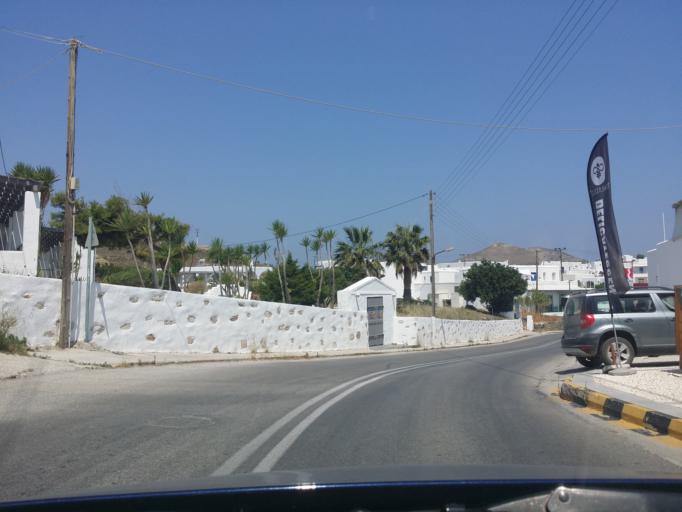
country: GR
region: South Aegean
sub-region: Nomos Kykladon
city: Naousa
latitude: 37.1192
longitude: 25.2331
